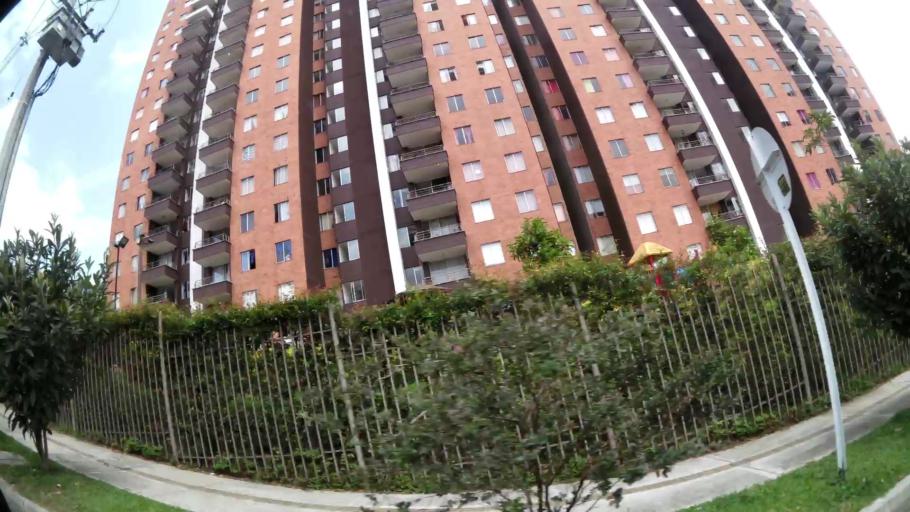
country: CO
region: Antioquia
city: Itagui
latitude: 6.1946
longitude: -75.5998
